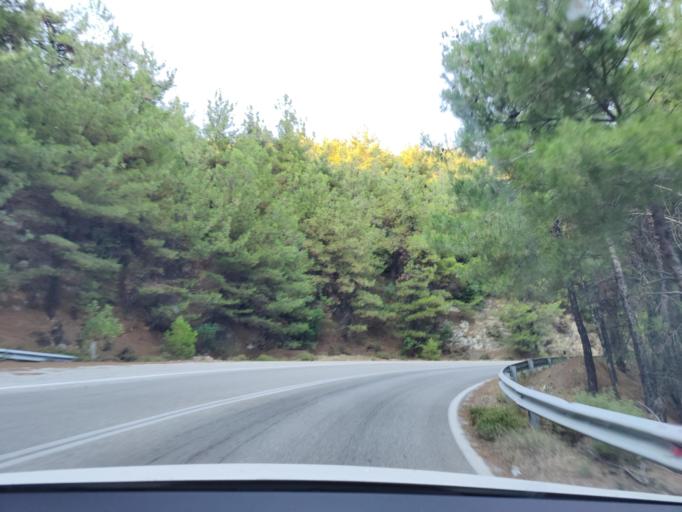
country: GR
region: East Macedonia and Thrace
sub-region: Nomos Kavalas
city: Potamia
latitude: 40.6283
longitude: 24.7646
